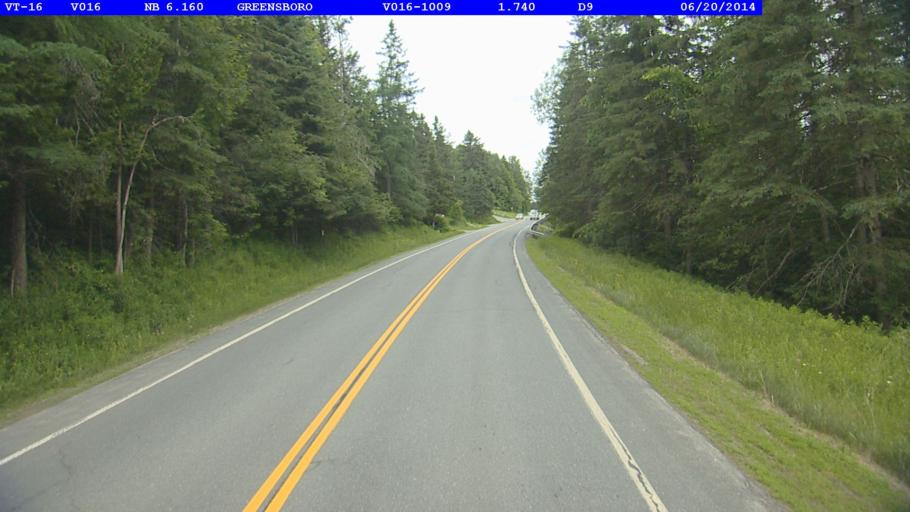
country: US
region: Vermont
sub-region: Caledonia County
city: Hardwick
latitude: 44.5667
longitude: -72.2525
